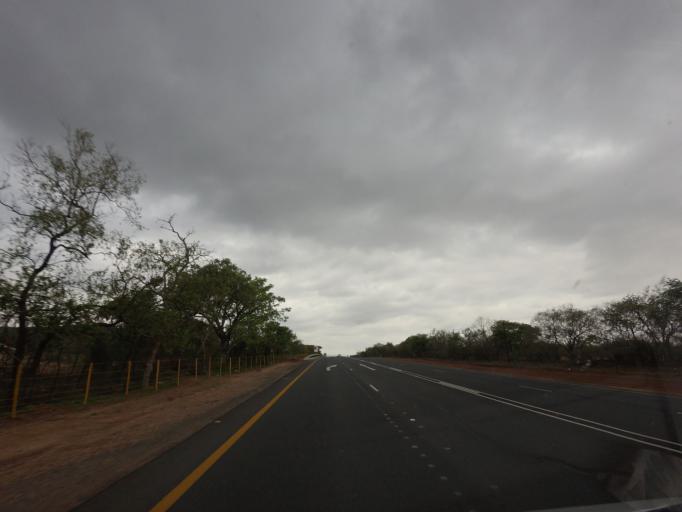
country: ZA
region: Mpumalanga
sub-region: Ehlanzeni District
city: Komatipoort
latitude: -25.4396
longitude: 31.7710
